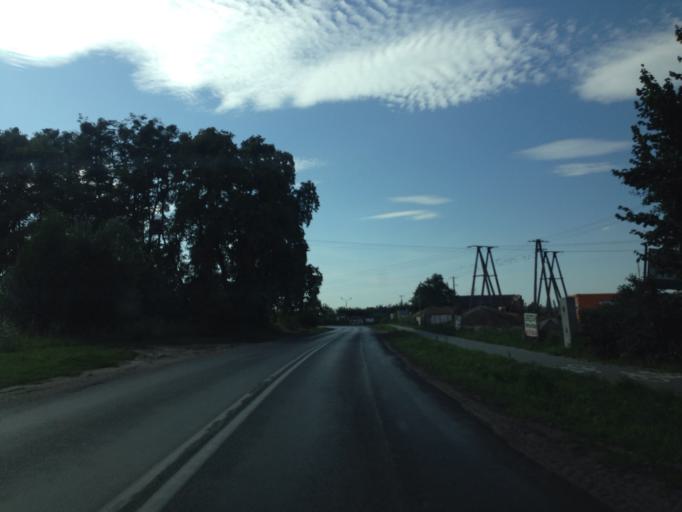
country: PL
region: Kujawsko-Pomorskie
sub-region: Powiat aleksandrowski
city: Aleksandrow Kujawski
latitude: 52.8665
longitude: 18.7137
